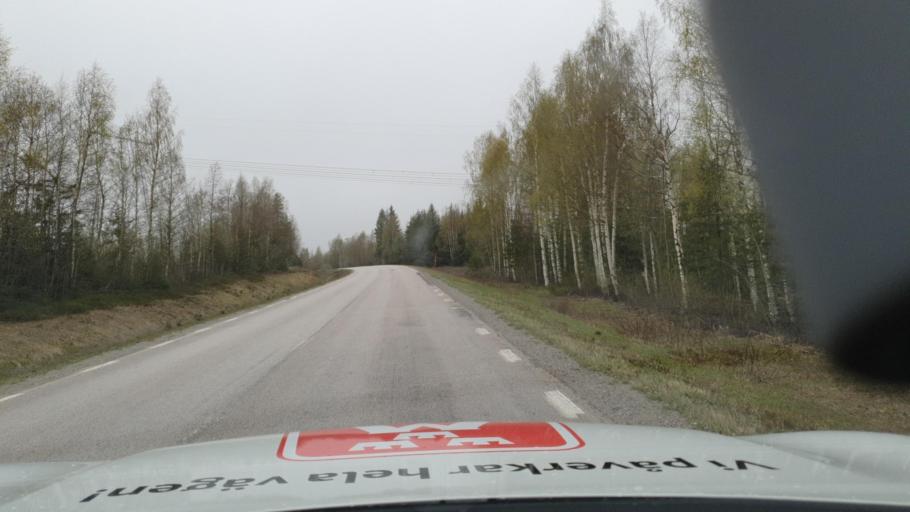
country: SE
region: Vaesterbotten
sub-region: Vannas Kommun
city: Vaennaes
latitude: 63.7949
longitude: 19.8075
